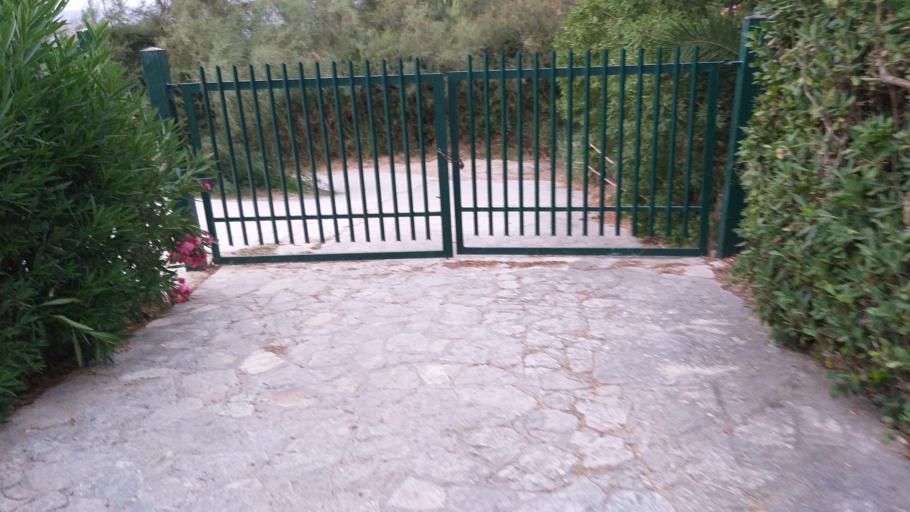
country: IT
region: Sicily
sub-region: Trapani
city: Castelluzzo
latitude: 38.0785
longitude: 12.8130
